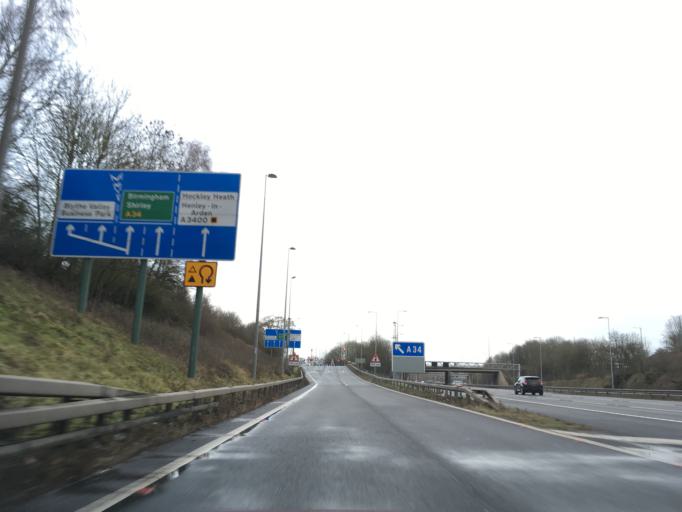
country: GB
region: England
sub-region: Solihull
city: Cheswick Green
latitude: 52.3772
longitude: -1.7886
